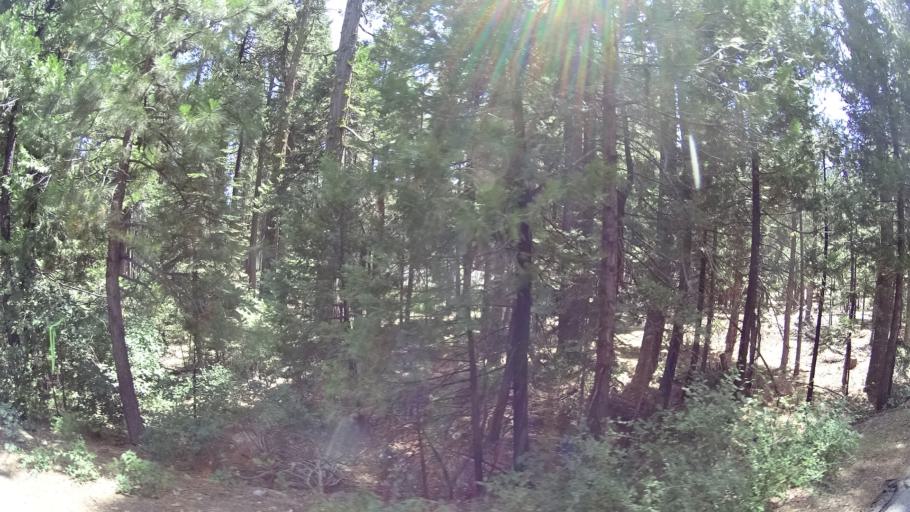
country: US
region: California
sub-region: Calaveras County
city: Arnold
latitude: 38.3038
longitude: -120.2636
